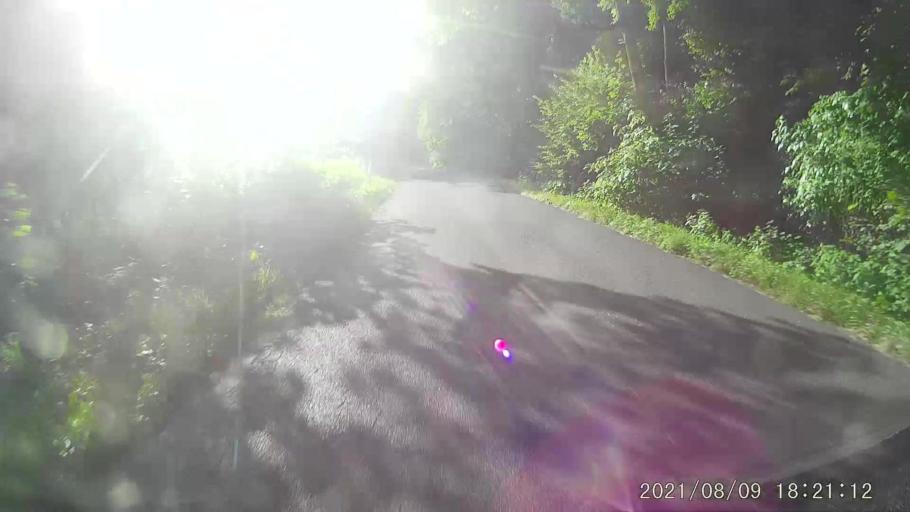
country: PL
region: Lower Silesian Voivodeship
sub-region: Powiat zabkowicki
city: Bardo
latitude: 50.5106
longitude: 16.6972
